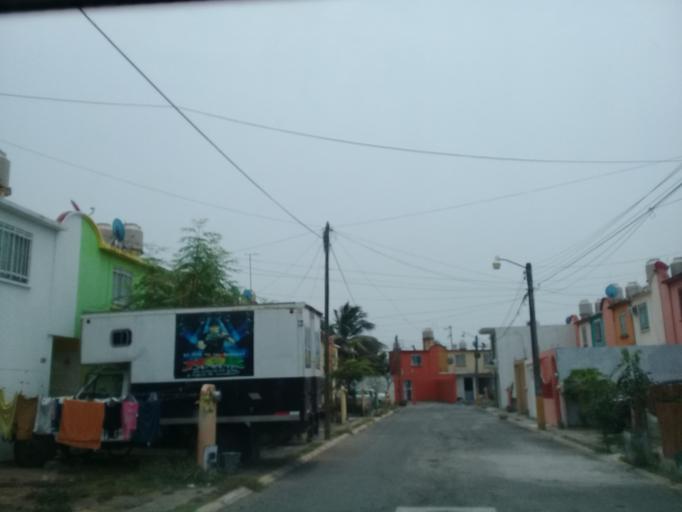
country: MX
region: Veracruz
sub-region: Veracruz
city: Las Amapolas
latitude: 19.1516
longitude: -96.2043
